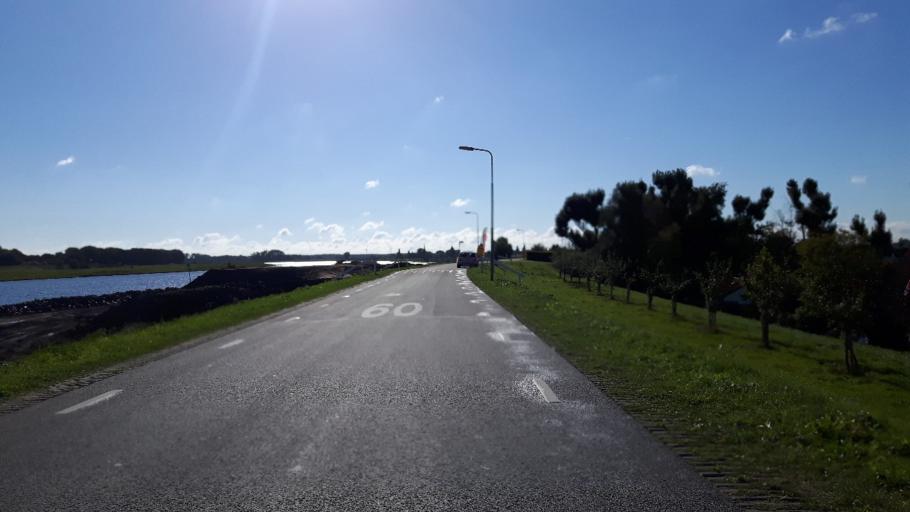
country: NL
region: Utrecht
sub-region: Gemeente Vianen
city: Vianen
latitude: 51.9796
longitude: 5.1424
